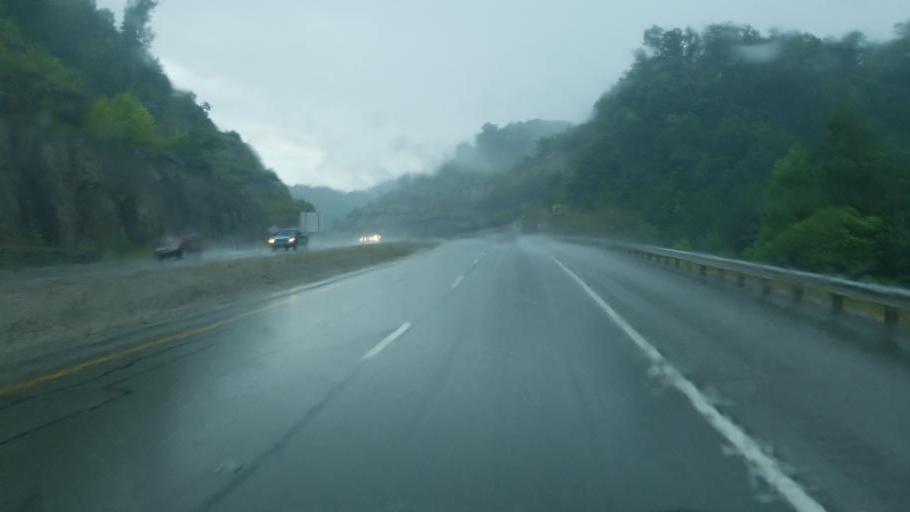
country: US
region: Kentucky
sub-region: Pike County
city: Pikeville
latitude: 37.5758
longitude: -82.4156
